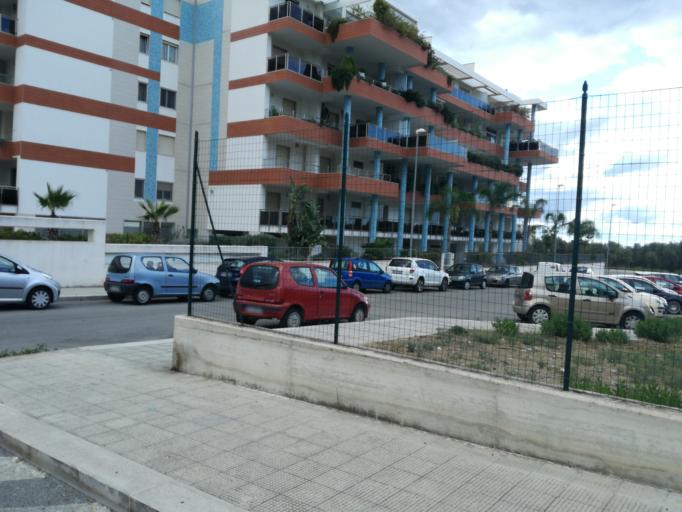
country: IT
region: Apulia
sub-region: Provincia di Bari
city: Triggiano
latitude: 41.0711
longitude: 16.9324
